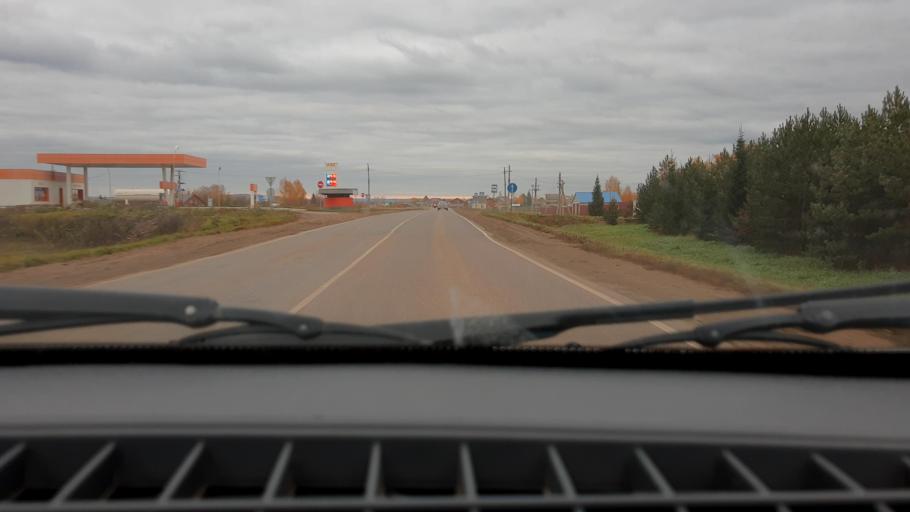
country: RU
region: Bashkortostan
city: Kabakovo
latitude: 54.5472
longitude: 56.0860
